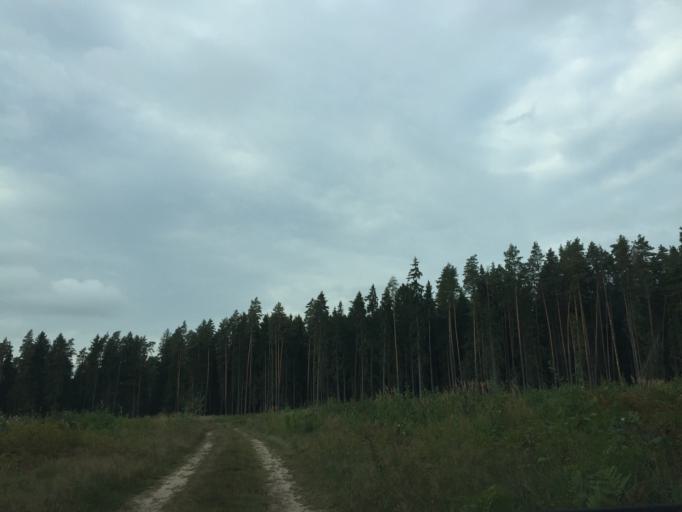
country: LV
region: Baldone
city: Baldone
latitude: 56.7745
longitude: 24.4472
